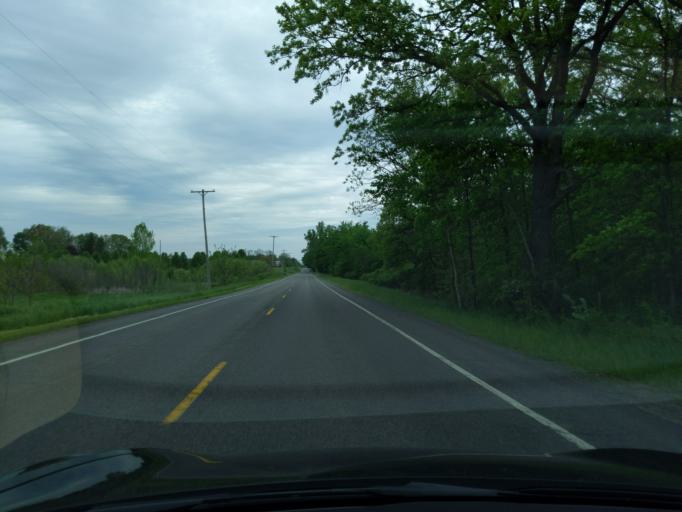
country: US
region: Michigan
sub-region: Ingham County
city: Mason
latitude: 42.5594
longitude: -84.3568
